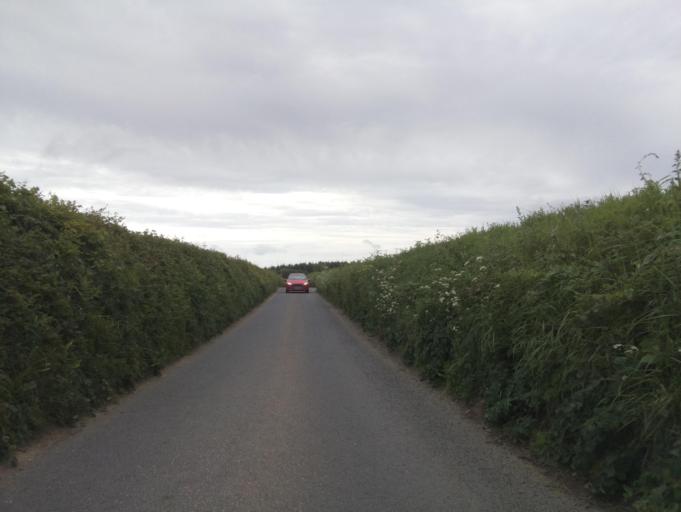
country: GB
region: England
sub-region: Devon
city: Dartmouth
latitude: 50.3368
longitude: -3.6506
